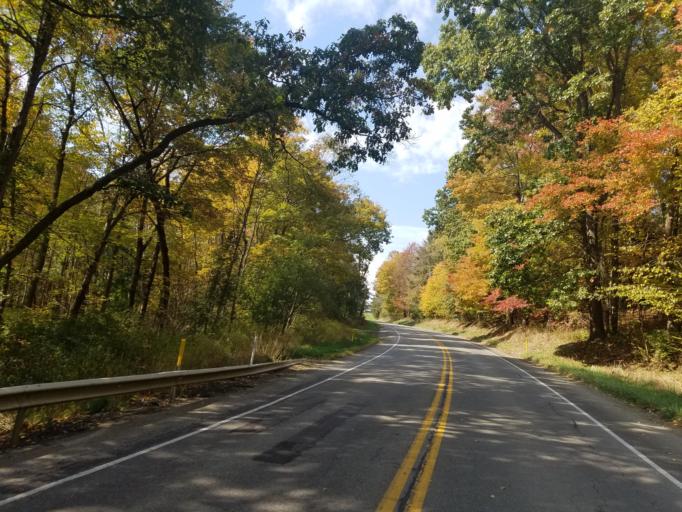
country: US
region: Pennsylvania
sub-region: Clarion County
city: Knox
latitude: 41.2340
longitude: -79.5902
